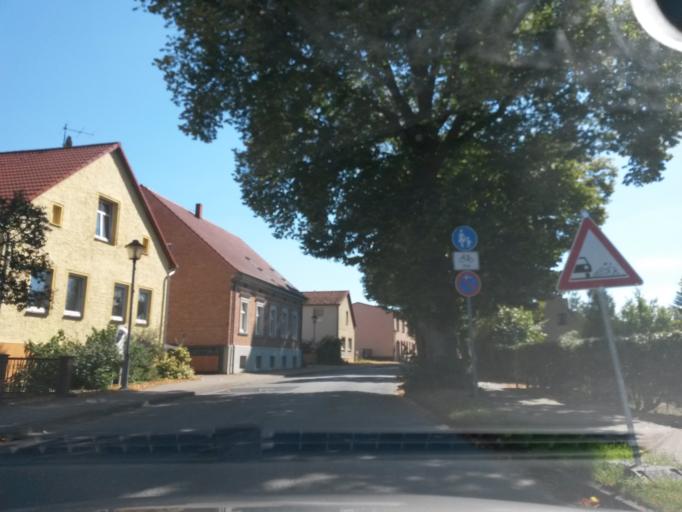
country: DE
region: Brandenburg
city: Lychen
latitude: 53.2156
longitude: 13.3126
